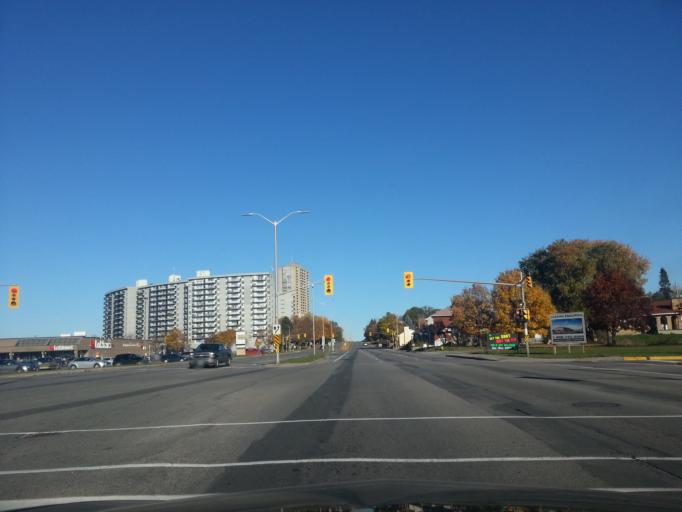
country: CA
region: Ontario
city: Ottawa
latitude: 45.3708
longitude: -75.7692
